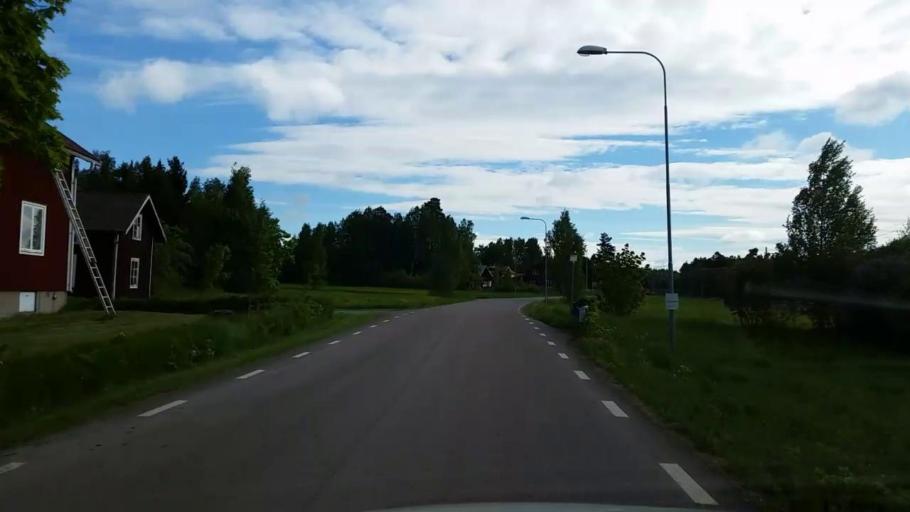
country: SE
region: Dalarna
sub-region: Borlange Kommun
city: Ornas
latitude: 60.5085
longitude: 15.5916
